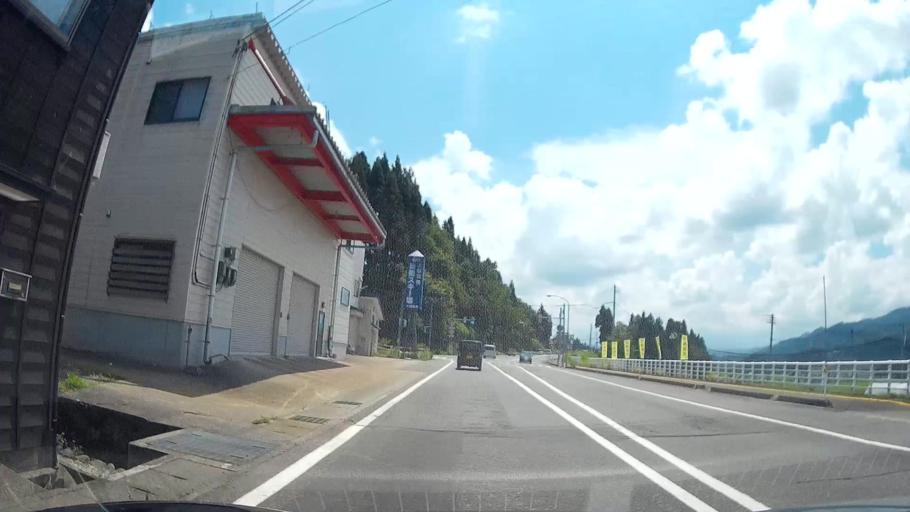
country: JP
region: Niigata
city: Tokamachi
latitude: 37.0824
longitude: 138.7220
